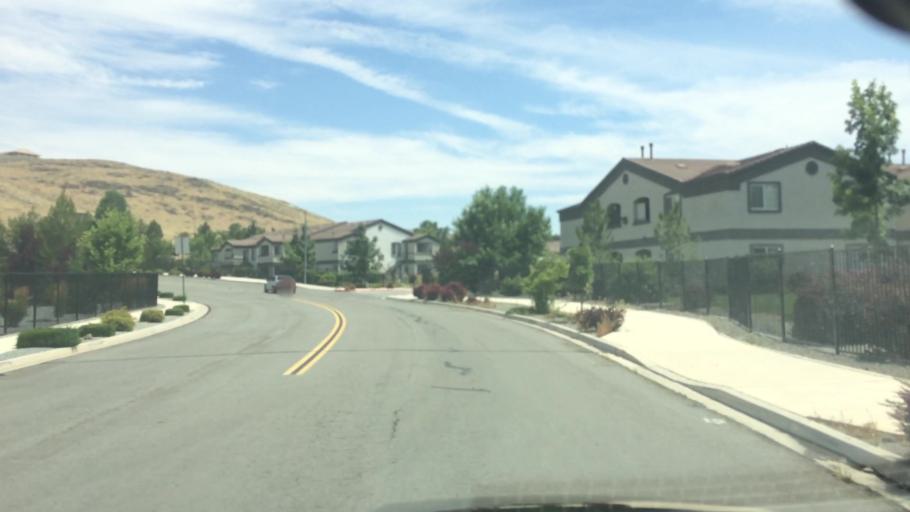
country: US
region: Nevada
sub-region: Washoe County
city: Spanish Springs
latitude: 39.5943
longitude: -119.7165
